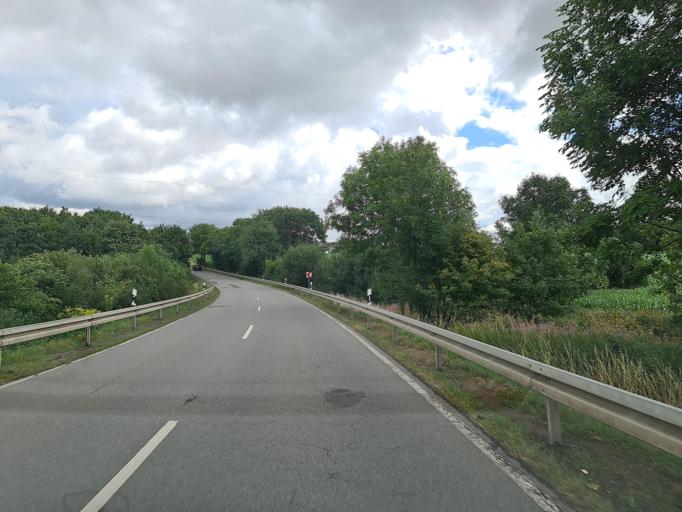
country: DE
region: Saxony
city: Niederwiesa
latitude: 50.8212
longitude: 13.0130
